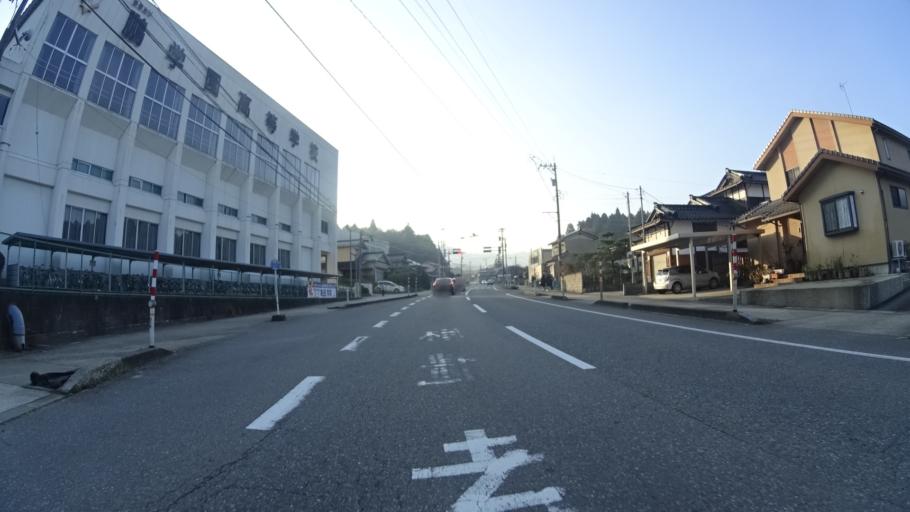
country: JP
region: Ishikawa
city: Nanao
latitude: 37.0301
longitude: 136.9731
